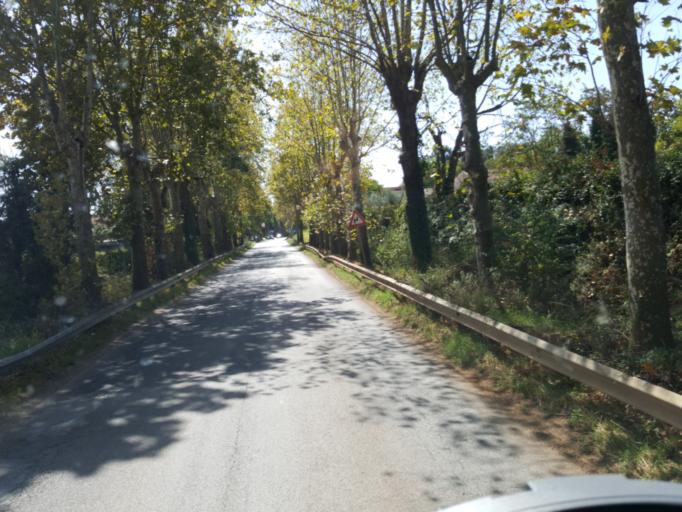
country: IT
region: Latium
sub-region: Provincia di Latina
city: Priverno
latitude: 41.4269
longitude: 13.1853
